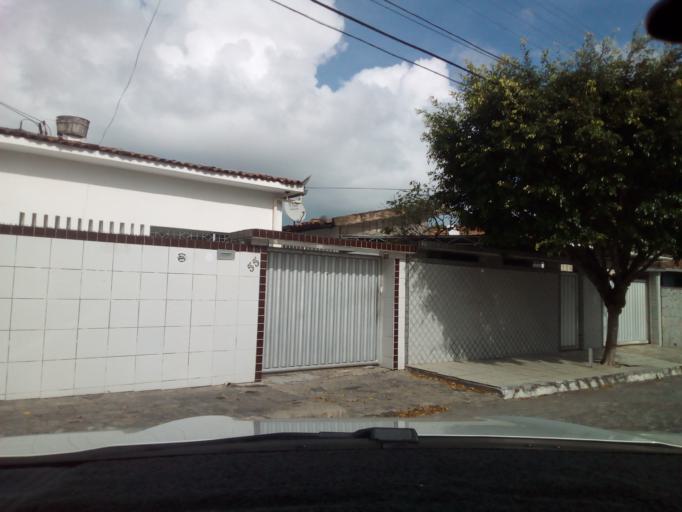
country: BR
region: Paraiba
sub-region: Joao Pessoa
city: Joao Pessoa
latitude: -7.1672
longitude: -34.8404
